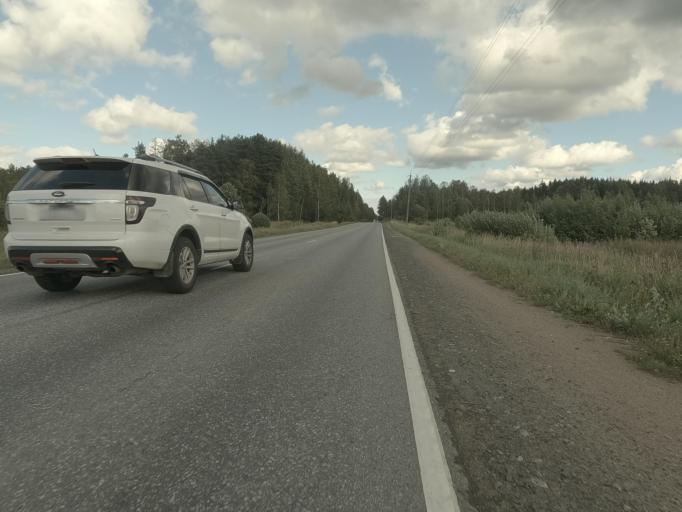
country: RU
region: Leningrad
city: Shcheglovo
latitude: 60.0286
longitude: 30.7928
